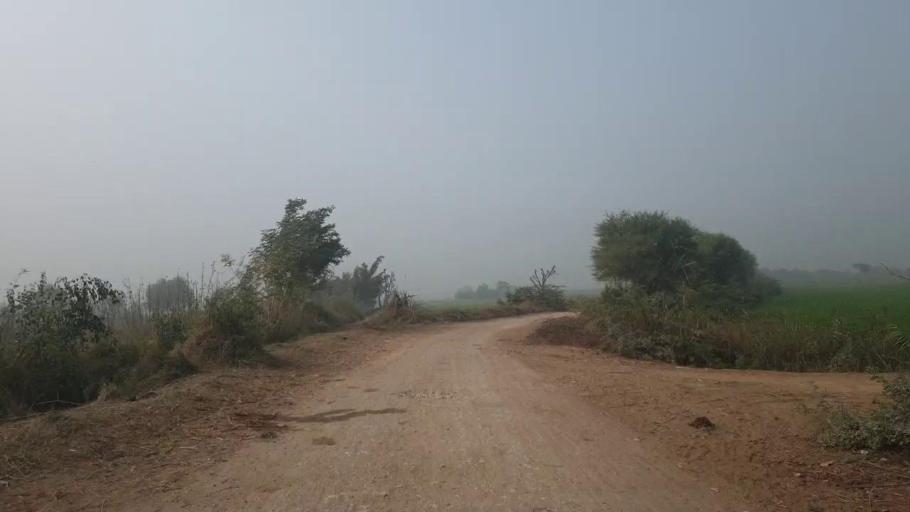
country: PK
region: Sindh
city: Bhit Shah
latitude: 25.8057
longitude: 68.5628
